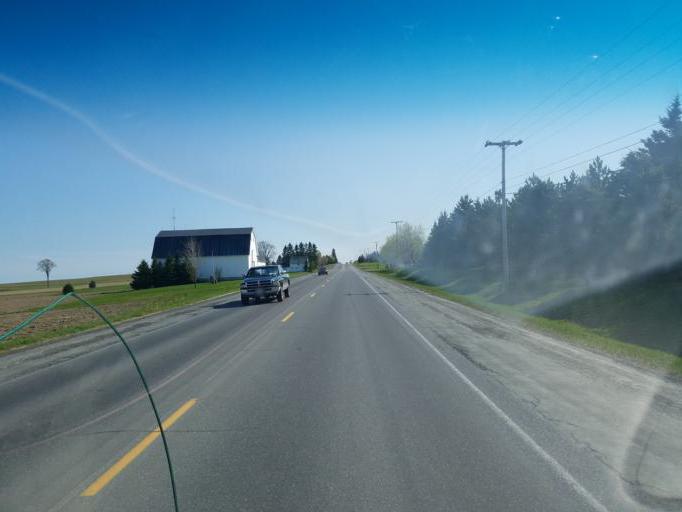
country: US
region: Maine
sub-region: Aroostook County
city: Presque Isle
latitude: 46.7342
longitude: -68.0003
